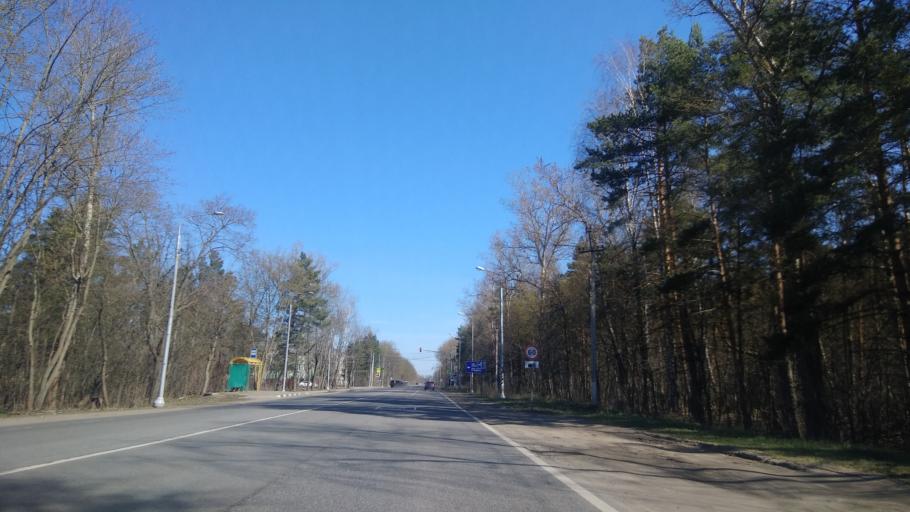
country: RU
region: Moskovskaya
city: Pushkino
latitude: 56.0307
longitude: 37.8709
